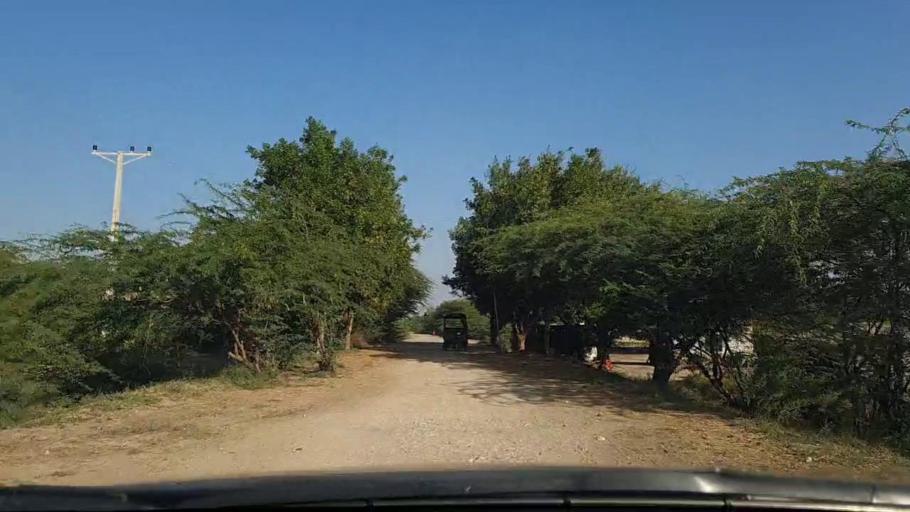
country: PK
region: Sindh
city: Mirpur Sakro
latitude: 24.5403
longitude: 67.6379
